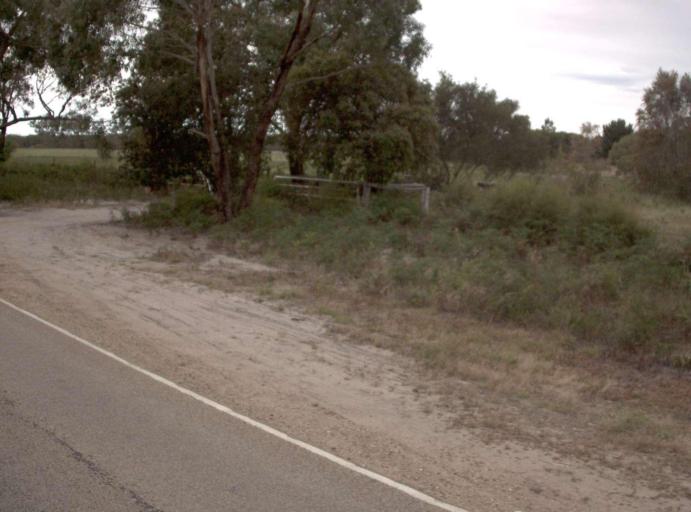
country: AU
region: Victoria
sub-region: Wellington
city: Sale
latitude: -38.0053
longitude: 147.2740
